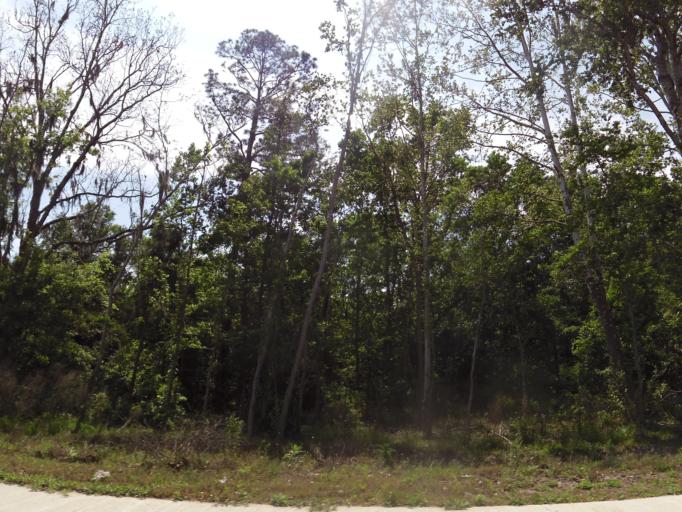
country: US
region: Florida
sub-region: Nassau County
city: Yulee
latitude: 30.5178
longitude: -81.6459
